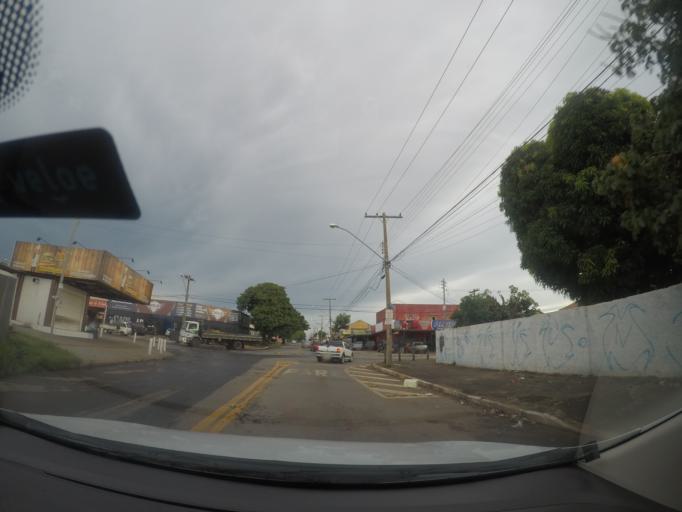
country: BR
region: Goias
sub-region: Goiania
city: Goiania
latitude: -16.6980
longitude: -49.3077
